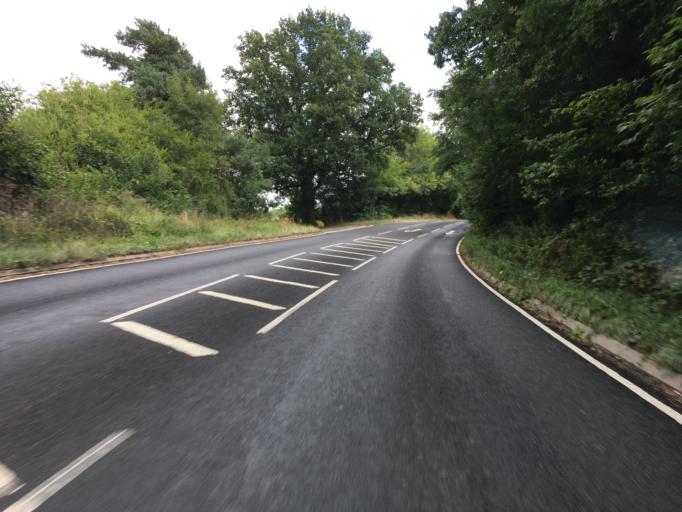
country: GB
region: England
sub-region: Kent
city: Cranbrook
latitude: 51.1132
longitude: 0.5314
